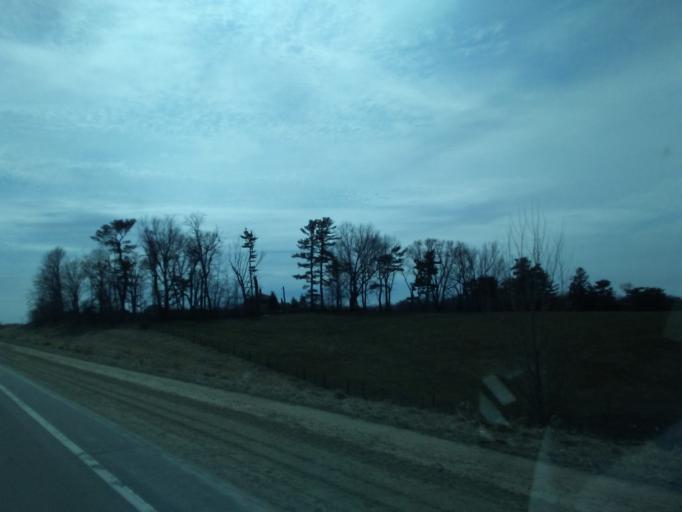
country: US
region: Iowa
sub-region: Winneshiek County
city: Decorah
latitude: 43.3507
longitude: -91.8053
